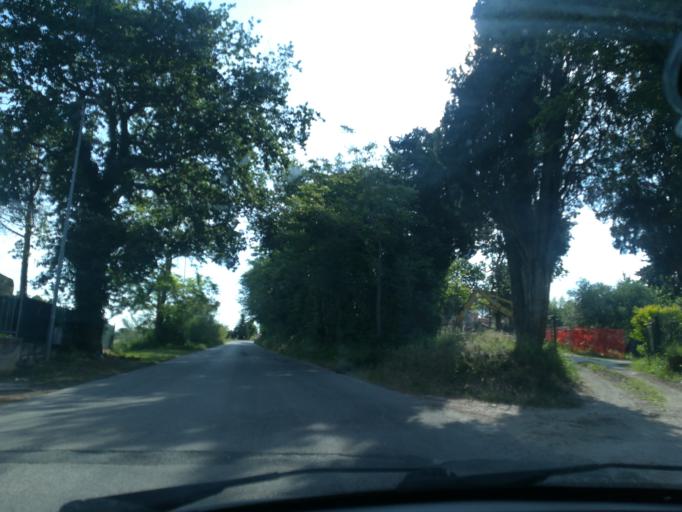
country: IT
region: The Marches
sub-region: Provincia di Macerata
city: Piediripa
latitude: 43.2956
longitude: 13.4781
